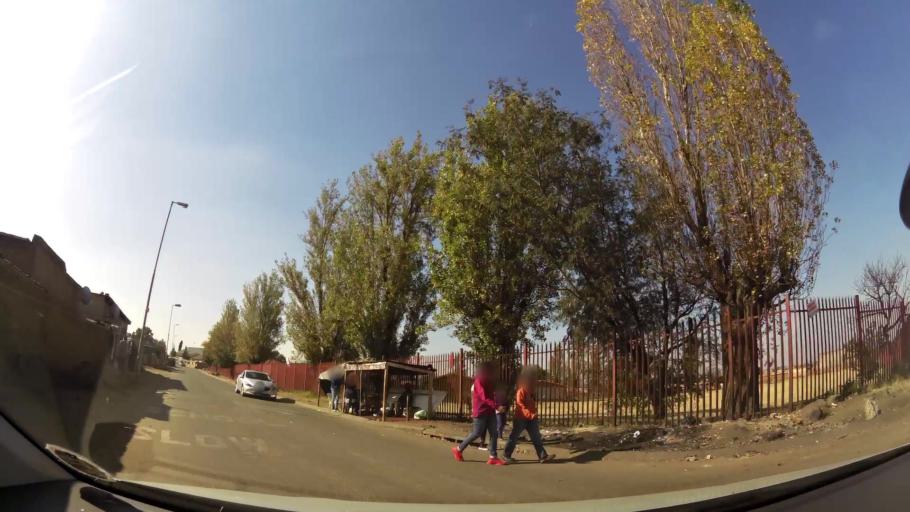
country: ZA
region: Gauteng
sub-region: City of Johannesburg Metropolitan Municipality
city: Soweto
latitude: -26.2822
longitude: 27.8668
